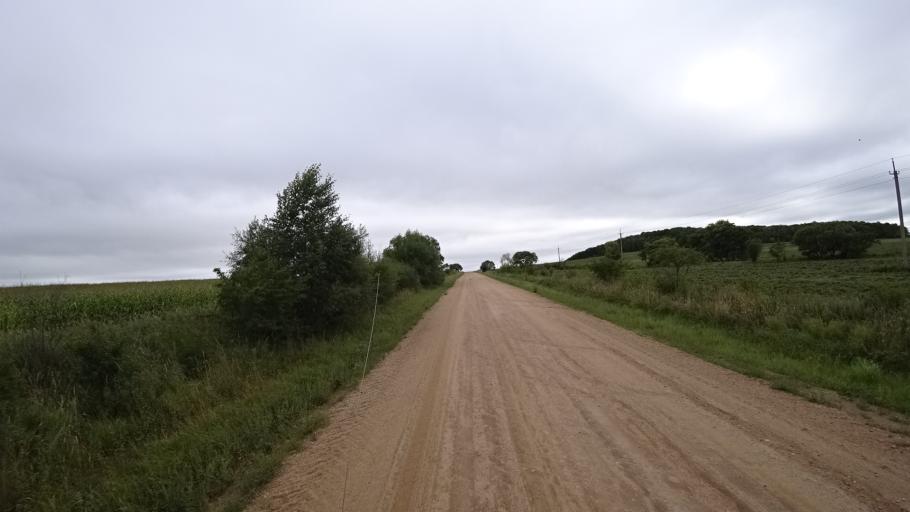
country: RU
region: Primorskiy
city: Monastyrishche
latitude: 44.0943
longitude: 132.6003
